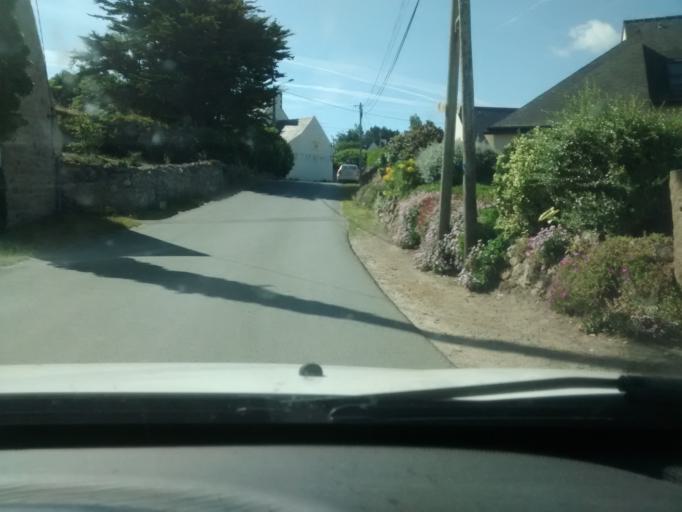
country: FR
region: Brittany
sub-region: Departement des Cotes-d'Armor
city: Trevou-Treguignec
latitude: 48.8262
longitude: -3.3420
